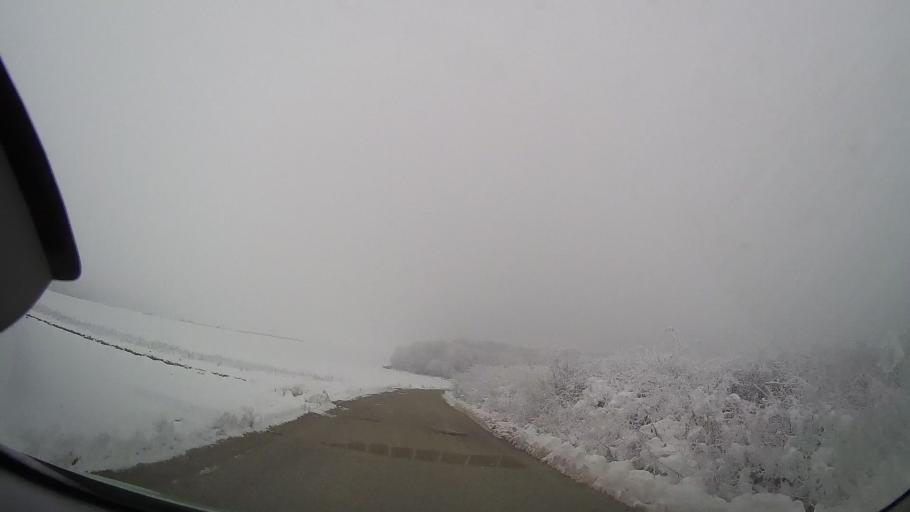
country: RO
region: Iasi
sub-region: Comuna Dagata
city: Dagata
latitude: 46.9078
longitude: 27.1888
